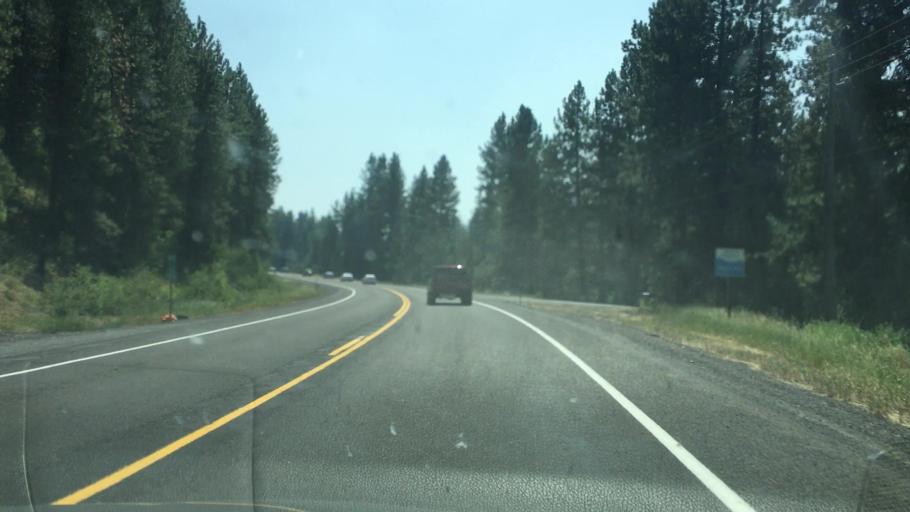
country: US
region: Idaho
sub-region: Valley County
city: McCall
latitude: 45.0986
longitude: -116.3075
